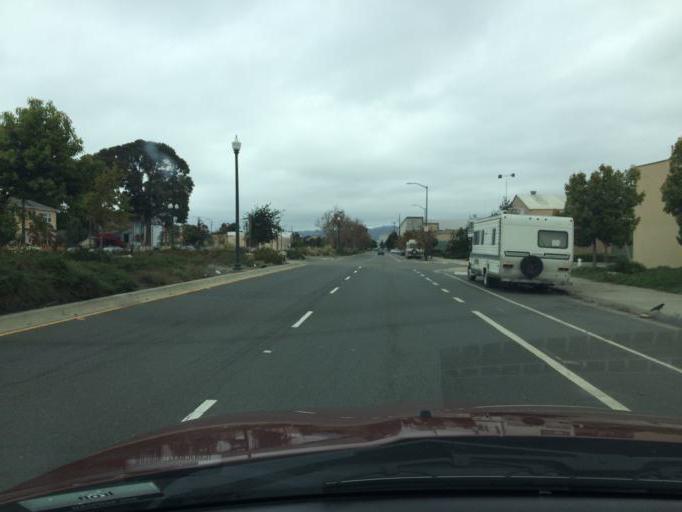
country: US
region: California
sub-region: Alameda County
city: Emeryville
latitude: 37.8117
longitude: -122.2910
